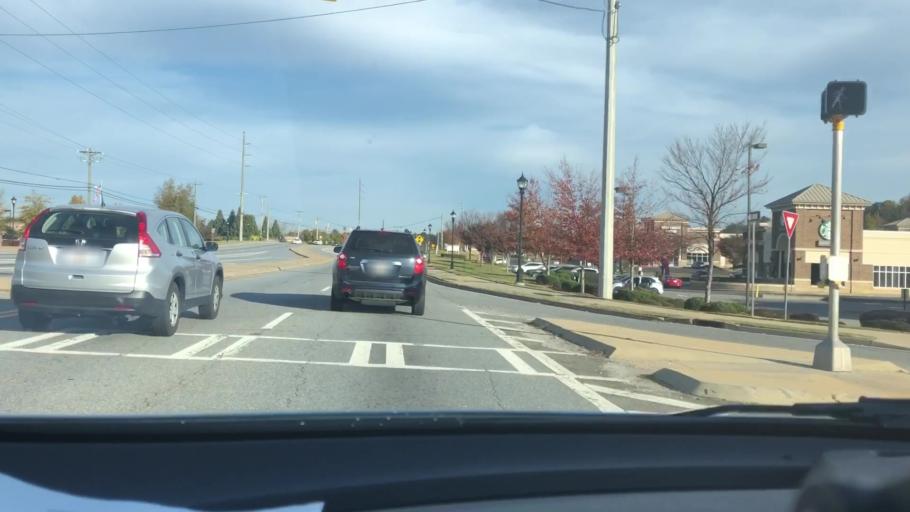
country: US
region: Georgia
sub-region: Forsyth County
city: Cumming
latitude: 34.1514
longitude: -84.1737
